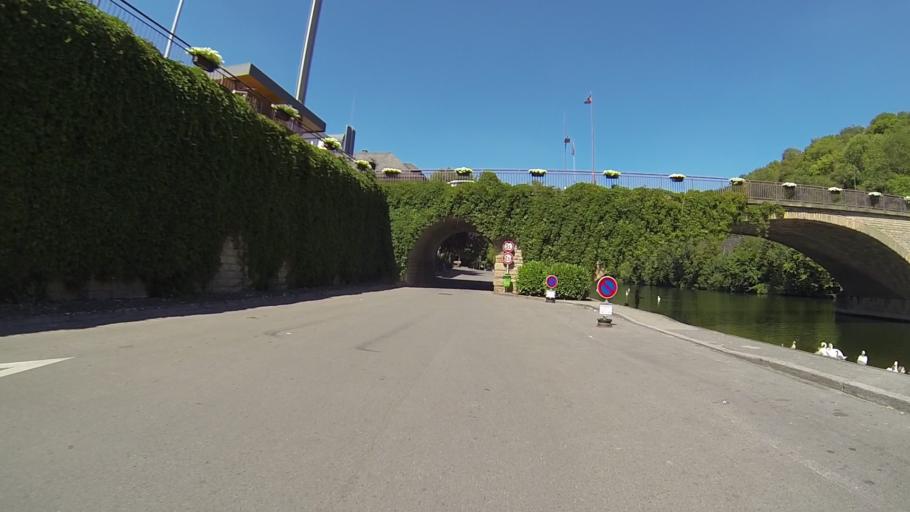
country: DE
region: Rheinland-Pfalz
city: Oberbillig
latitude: 49.7141
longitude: 6.5063
